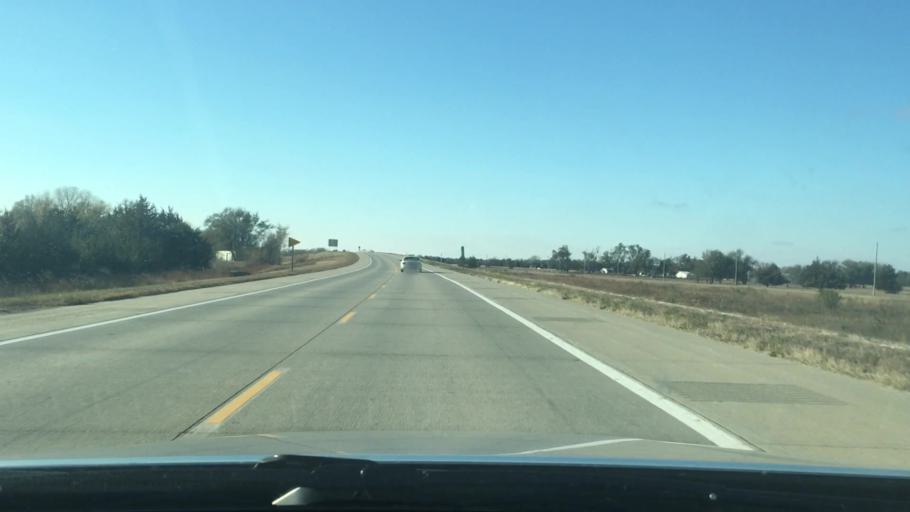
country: US
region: Kansas
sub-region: Reno County
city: Nickerson
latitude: 38.1000
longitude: -98.0097
